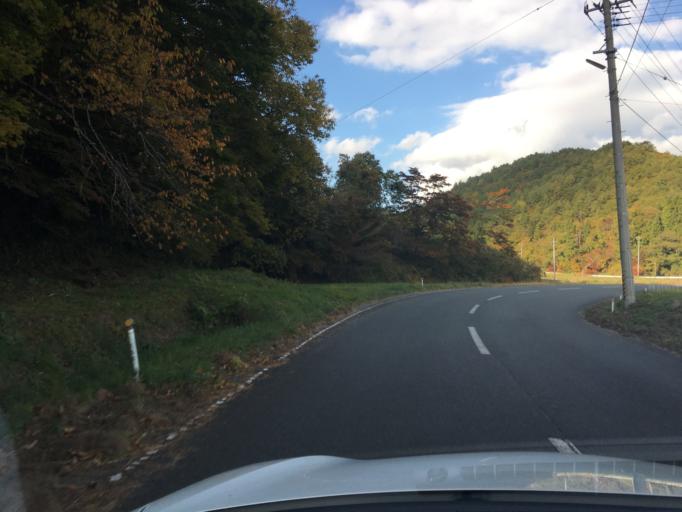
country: JP
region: Fukushima
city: Iwaki
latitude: 37.2311
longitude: 140.7638
